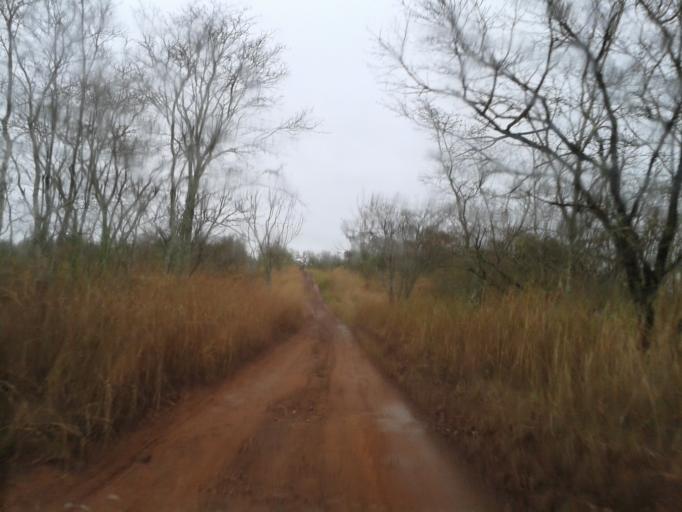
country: BR
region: Minas Gerais
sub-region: Campina Verde
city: Campina Verde
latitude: -19.3312
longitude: -49.5165
